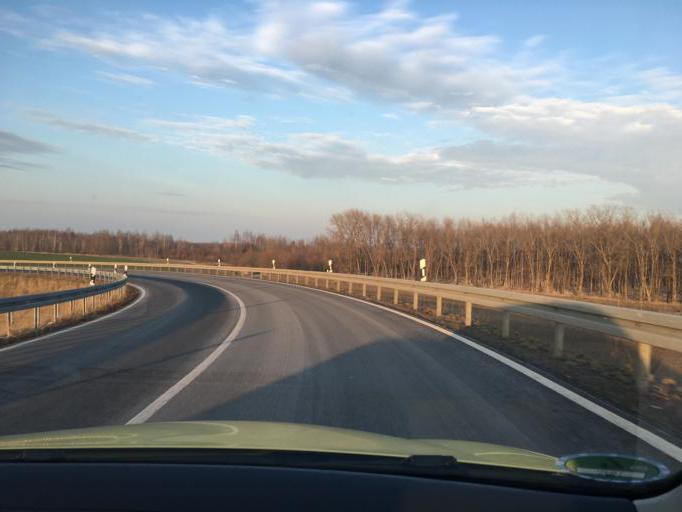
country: DE
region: Saxony
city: Borna
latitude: 51.1124
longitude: 12.5195
